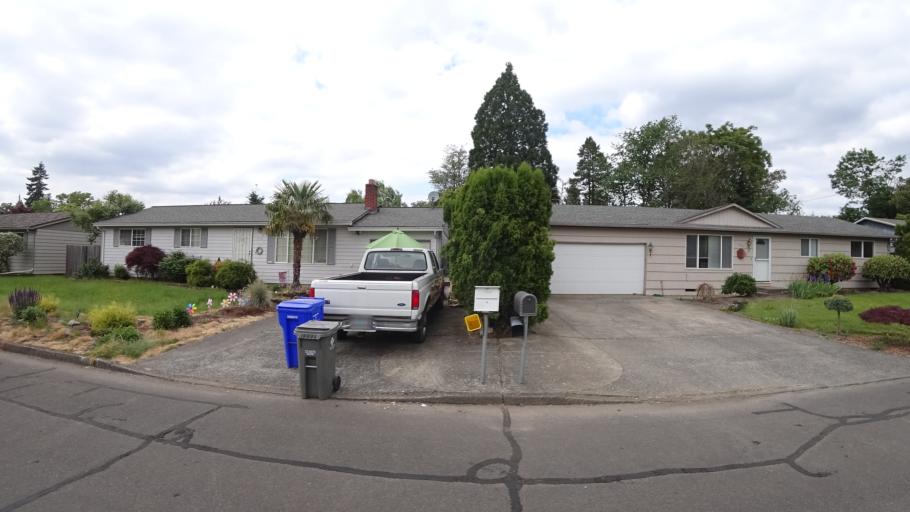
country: US
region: Oregon
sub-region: Multnomah County
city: Gresham
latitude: 45.5106
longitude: -122.4799
